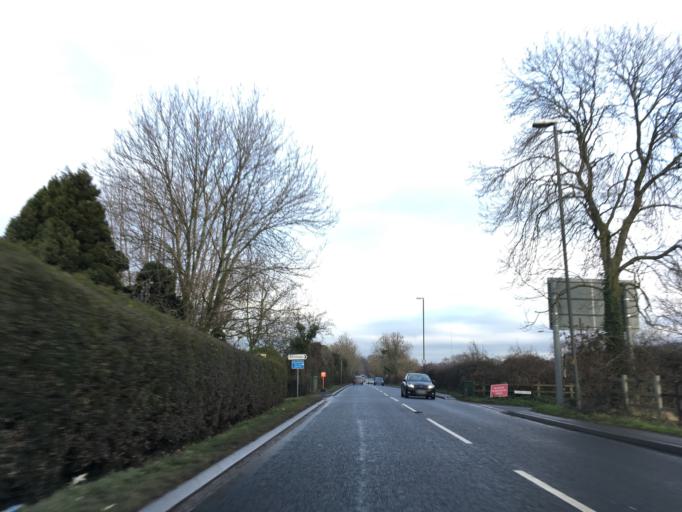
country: GB
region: England
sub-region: Gloucestershire
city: Shurdington
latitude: 51.8512
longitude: -2.1367
